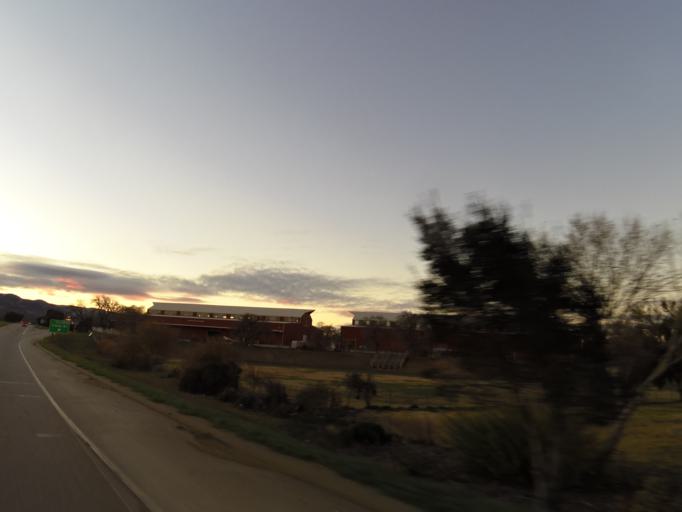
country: US
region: California
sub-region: Monterey County
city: King City
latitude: 36.2028
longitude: -121.1245
